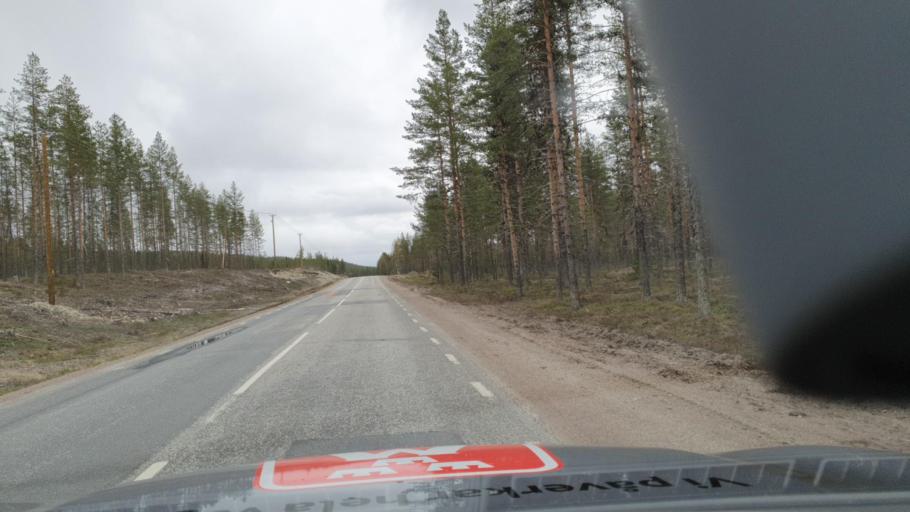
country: SE
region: Vaesternorrland
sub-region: Solleftea Kommun
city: Solleftea
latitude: 63.6341
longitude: 17.4259
